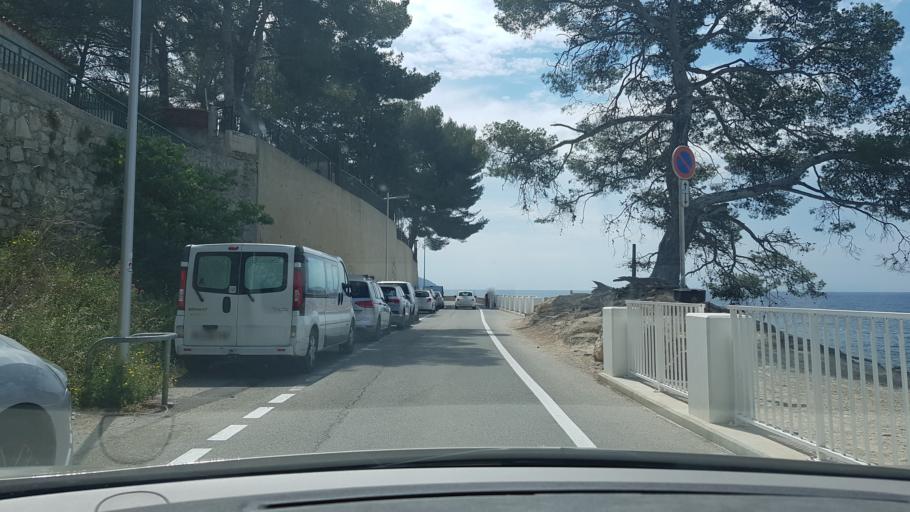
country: FR
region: Provence-Alpes-Cote d'Azur
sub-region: Departement des Bouches-du-Rhone
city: Ceyreste
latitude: 43.1886
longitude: 5.6444
